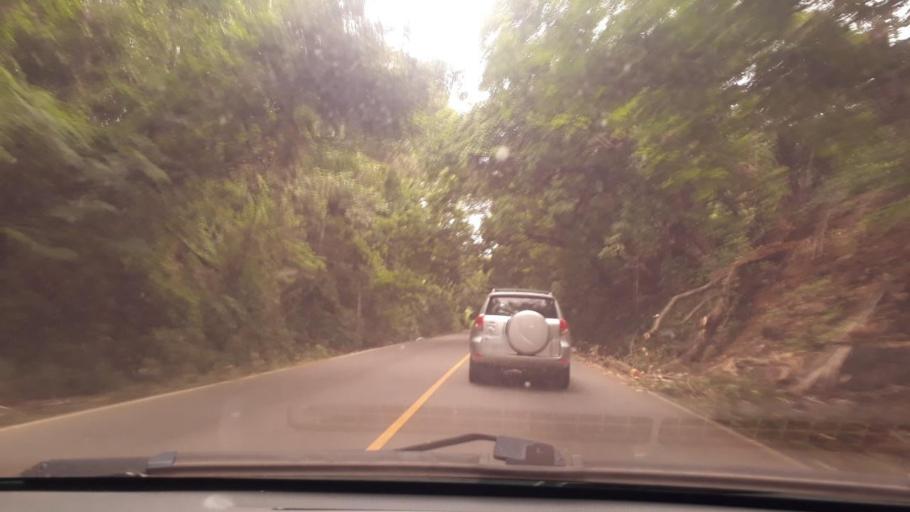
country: GT
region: Jutiapa
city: Asuncion Mita
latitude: 14.3555
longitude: -89.7582
